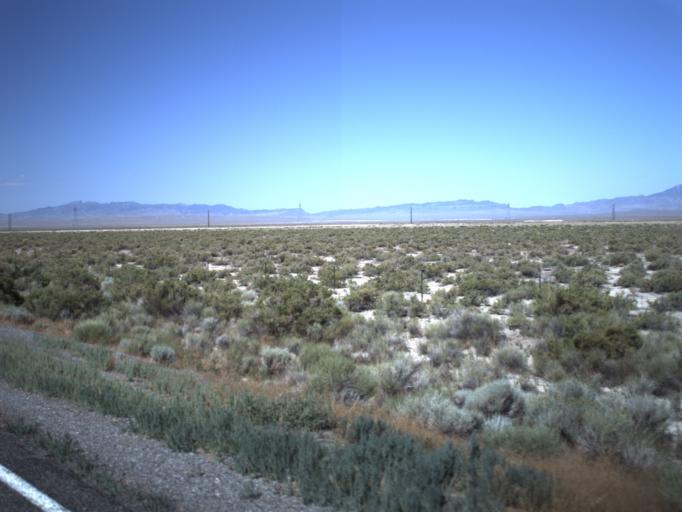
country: US
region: Utah
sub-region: Millard County
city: Delta
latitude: 39.2575
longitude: -112.8851
